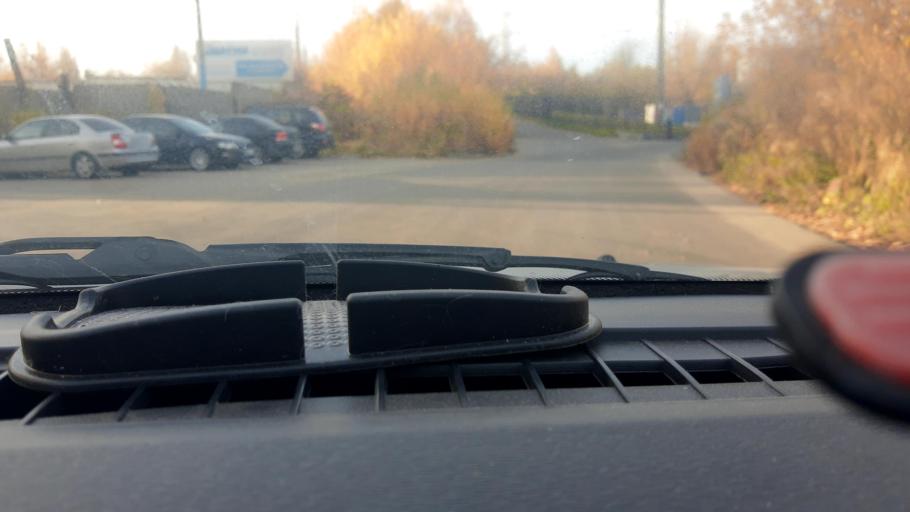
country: RU
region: Nizjnij Novgorod
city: Nizhniy Novgorod
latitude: 56.2461
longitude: 43.9948
